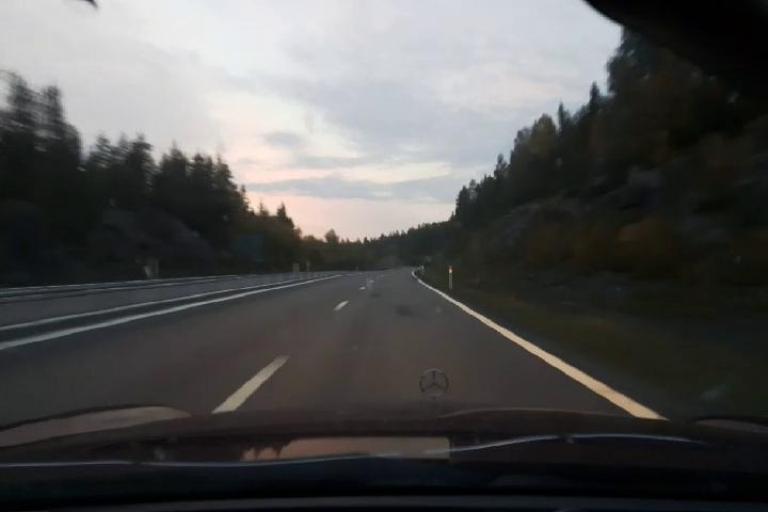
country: SE
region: Vaesternorrland
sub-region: Kramfors Kommun
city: Nordingra
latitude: 62.9427
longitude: 18.0941
